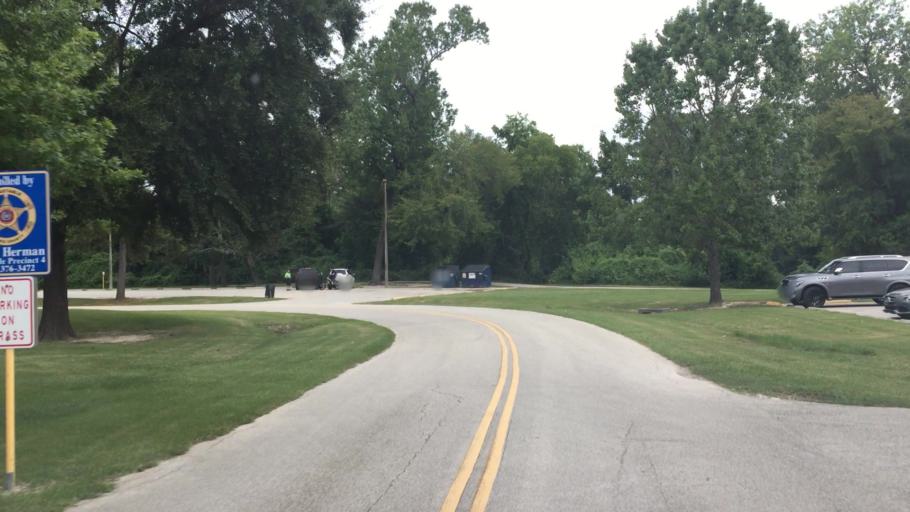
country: US
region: Texas
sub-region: Harris County
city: Hudson
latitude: 30.0105
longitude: -95.5103
